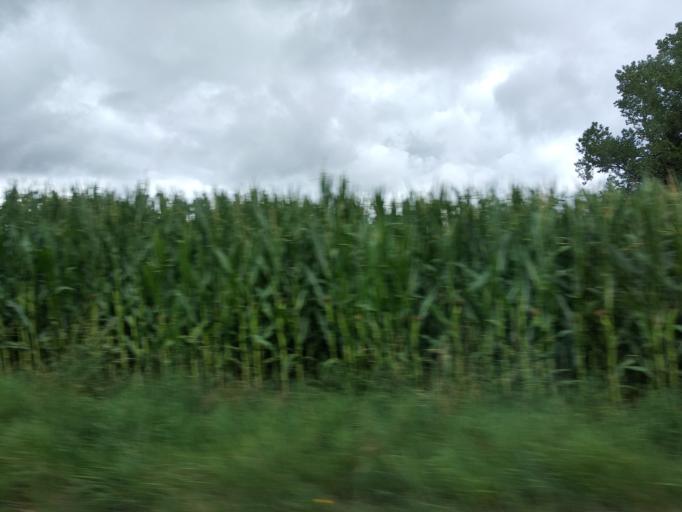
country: DE
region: Bavaria
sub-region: Swabia
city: Benningen
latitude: 47.9726
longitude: 10.2107
